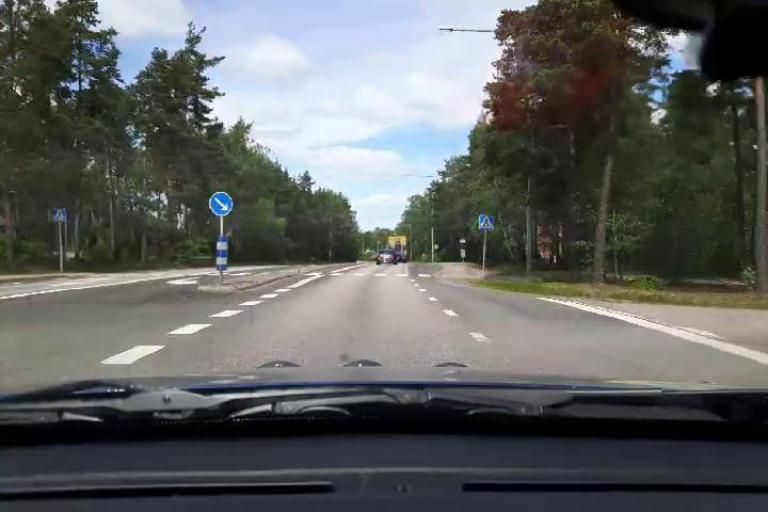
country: SE
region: Uppsala
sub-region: Osthammars Kommun
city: Bjorklinge
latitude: 60.0320
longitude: 17.5522
